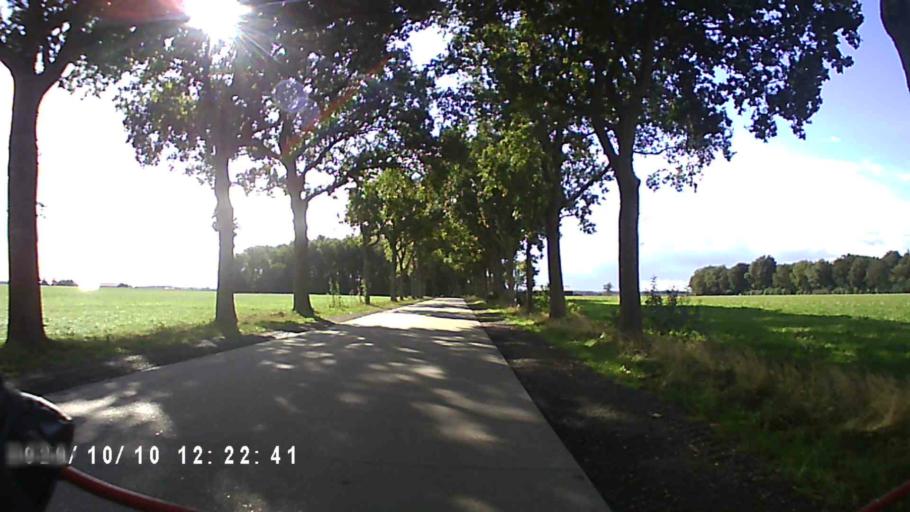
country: NL
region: Friesland
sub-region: Gemeente Heerenveen
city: Jubbega
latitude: 53.0002
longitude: 6.1802
